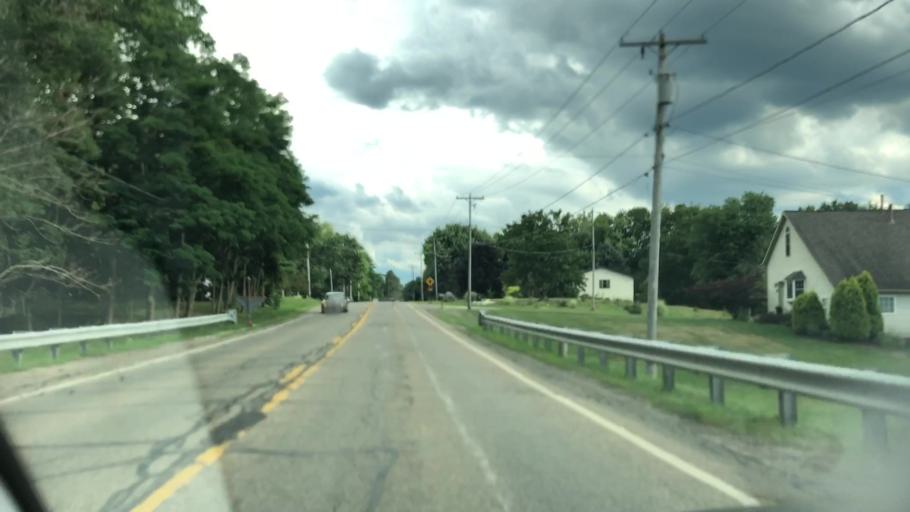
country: US
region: Ohio
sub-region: Summit County
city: Greensburg
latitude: 40.9239
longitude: -81.4638
